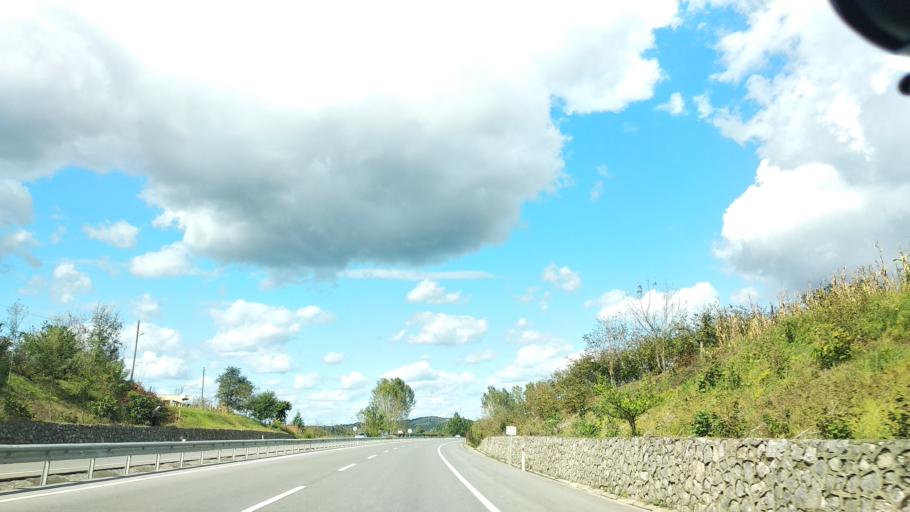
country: TR
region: Sakarya
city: Ortakoy
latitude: 41.0236
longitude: 30.6140
